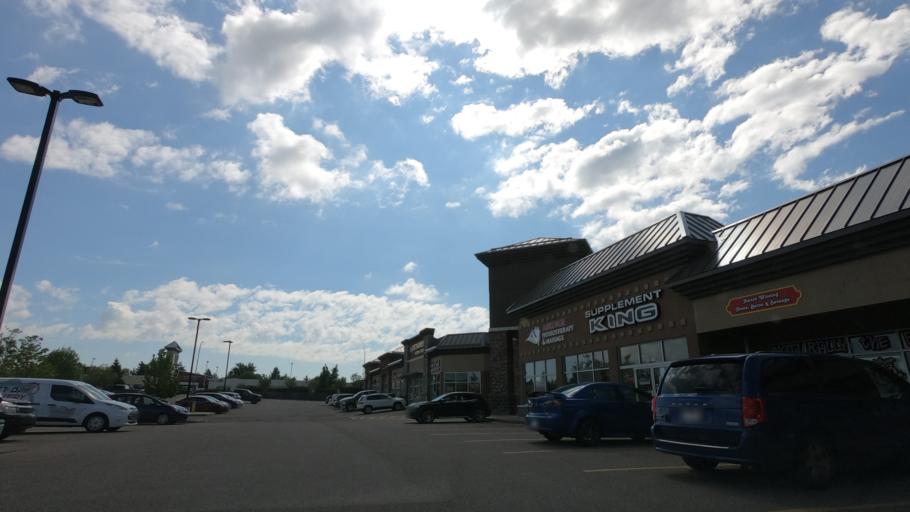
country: CA
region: Alberta
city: Airdrie
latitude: 51.2868
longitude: -114.0151
